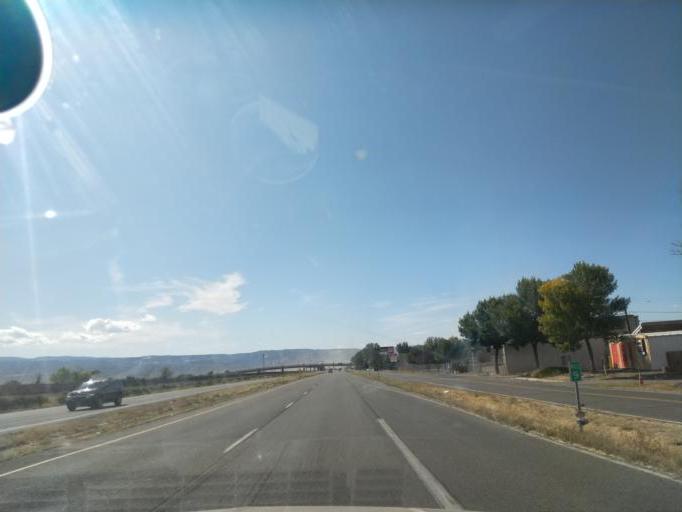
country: US
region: Colorado
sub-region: Mesa County
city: Fruitvale
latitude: 39.0754
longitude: -108.5048
